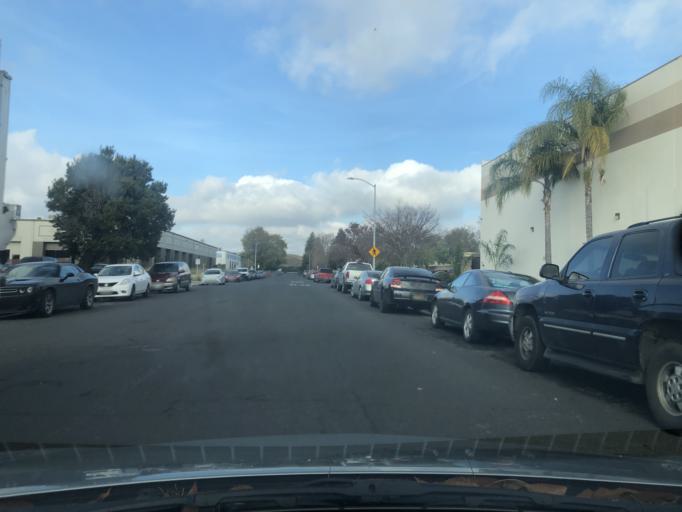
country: US
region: California
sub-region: Sacramento County
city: Rosemont
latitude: 38.5221
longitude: -121.3735
